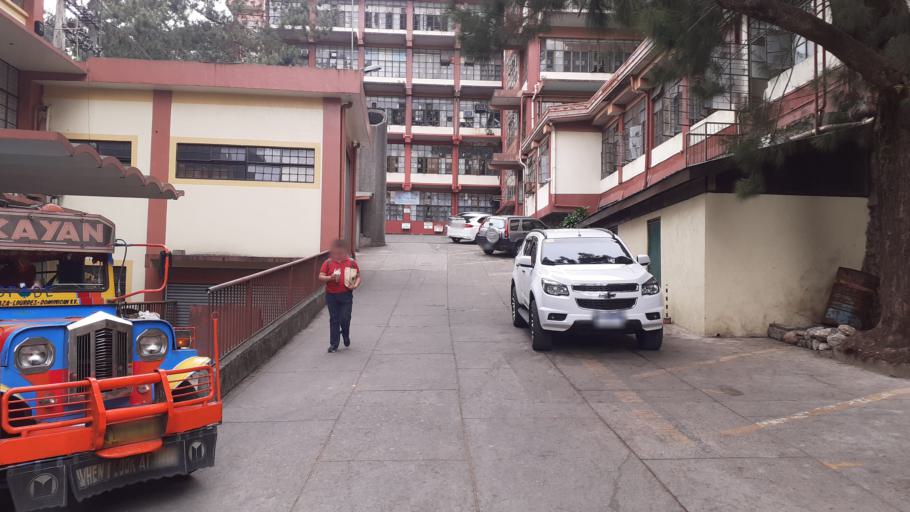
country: PH
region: Cordillera
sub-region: Baguio City
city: Baguio
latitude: 16.4175
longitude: 120.5982
